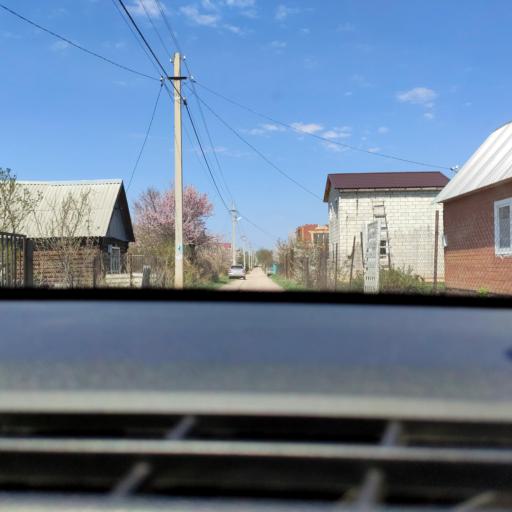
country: RU
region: Samara
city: Tol'yatti
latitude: 53.5929
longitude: 49.3007
